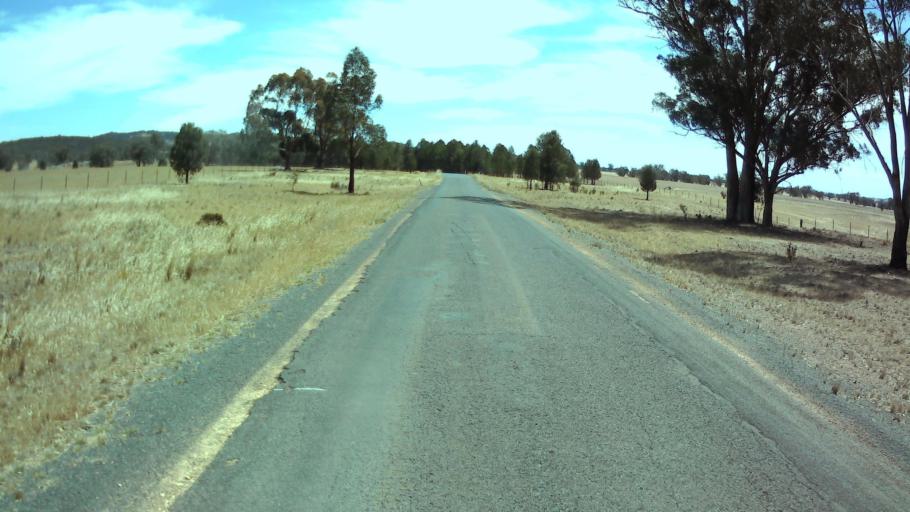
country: AU
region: New South Wales
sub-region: Weddin
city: Grenfell
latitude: -33.7739
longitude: 148.2069
